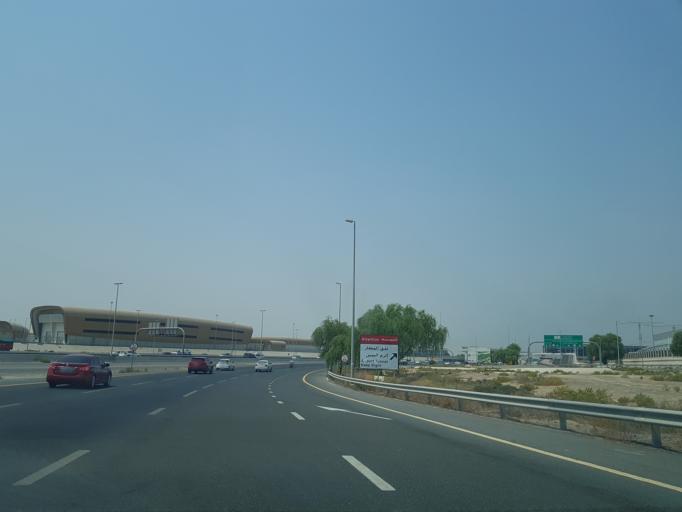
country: AE
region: Ash Shariqah
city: Sharjah
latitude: 25.2322
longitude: 55.4001
